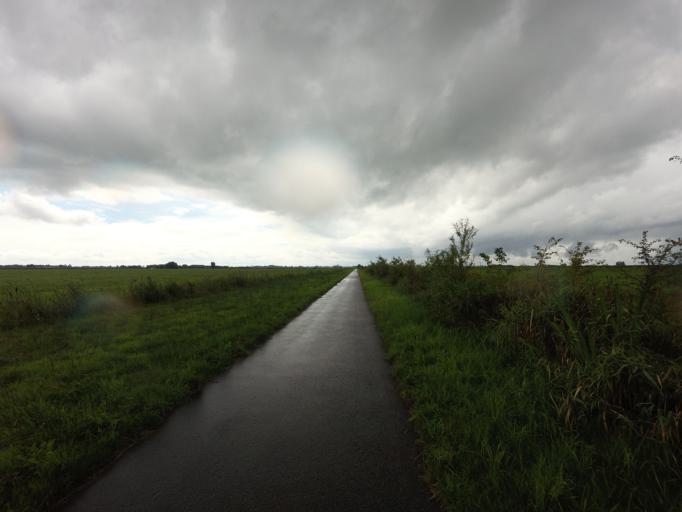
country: NL
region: North Holland
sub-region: Gemeente Wijdemeren
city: Nieuw-Loosdrecht
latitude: 52.1729
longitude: 5.1477
